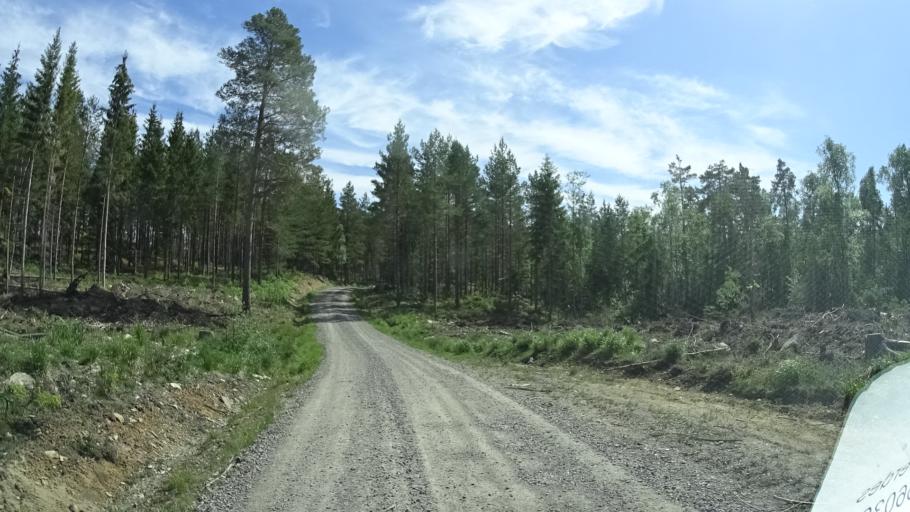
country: SE
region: OEstergoetland
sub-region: Norrkopings Kommun
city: Svartinge
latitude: 58.7832
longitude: 15.9104
